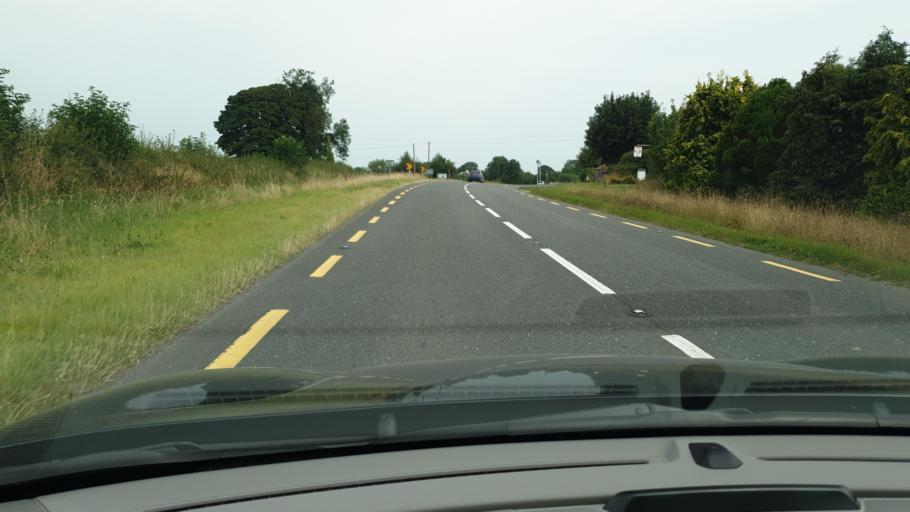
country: IE
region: Leinster
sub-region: An Mhi
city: Athboy
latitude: 53.6912
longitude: -6.9497
